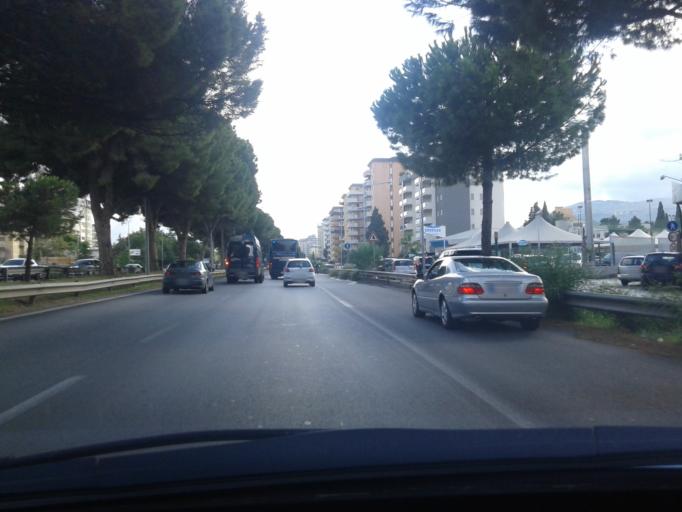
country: IT
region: Sicily
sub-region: Palermo
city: Palermo
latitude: 38.1359
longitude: 13.3306
